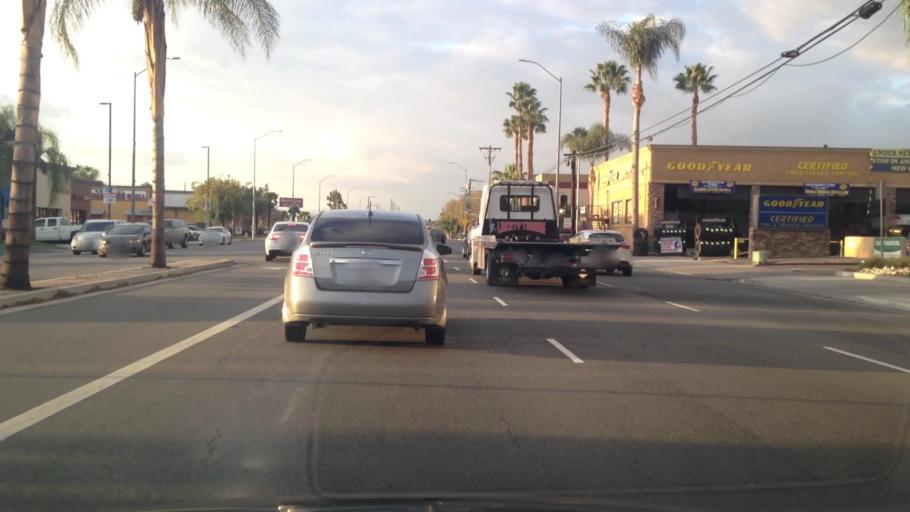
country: US
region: California
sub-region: Riverside County
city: Pedley
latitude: 33.9127
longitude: -117.4620
